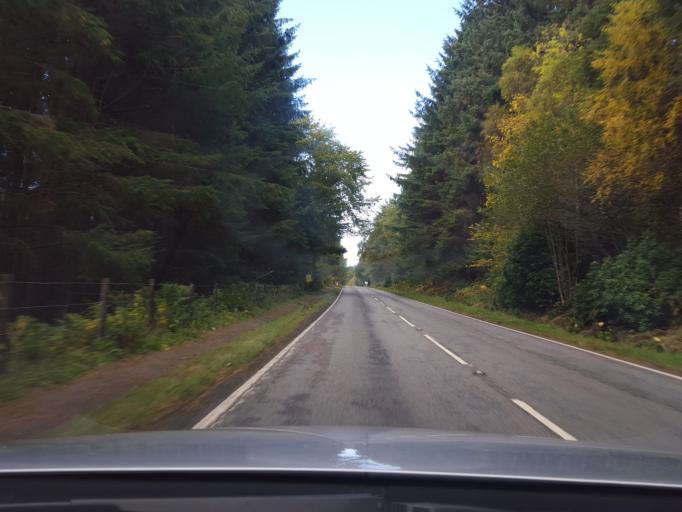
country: GB
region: Scotland
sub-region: Highland
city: Fort William
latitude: 57.2379
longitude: -5.4398
